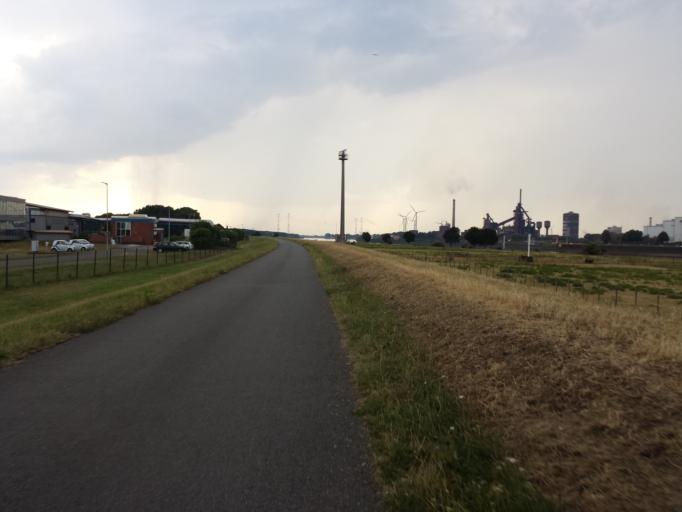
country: DE
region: Lower Saxony
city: Ritterhude
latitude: 53.1159
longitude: 8.7134
